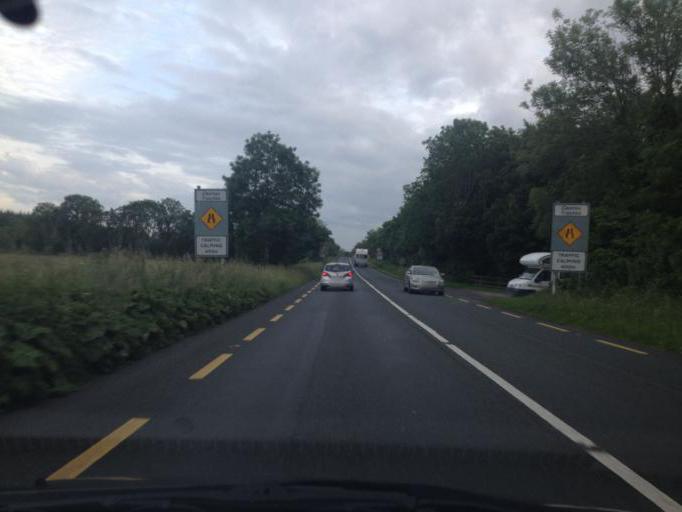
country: IE
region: Connaught
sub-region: Sligo
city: Sligo
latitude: 54.3355
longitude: -8.5022
